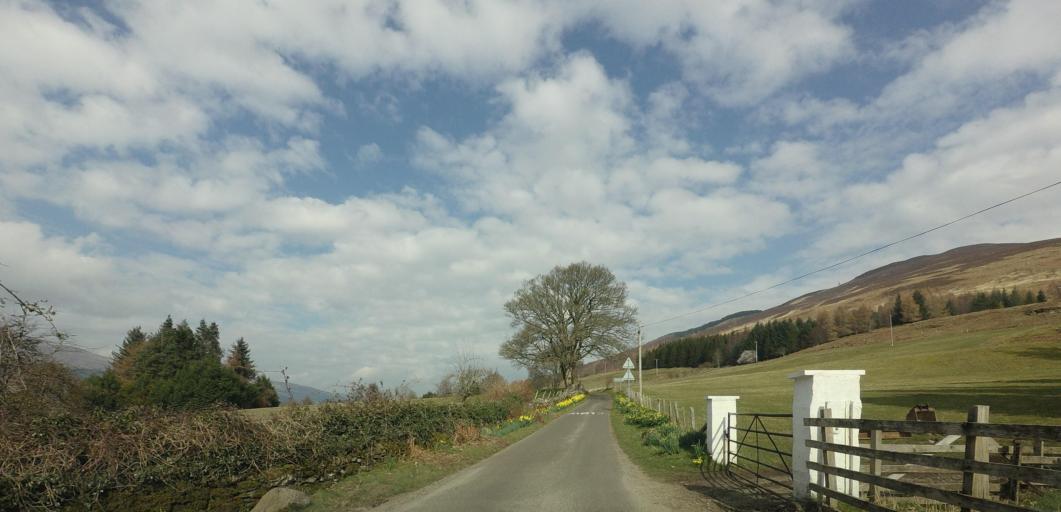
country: GB
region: Scotland
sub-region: Perth and Kinross
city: Comrie
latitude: 56.5280
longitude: -4.1118
